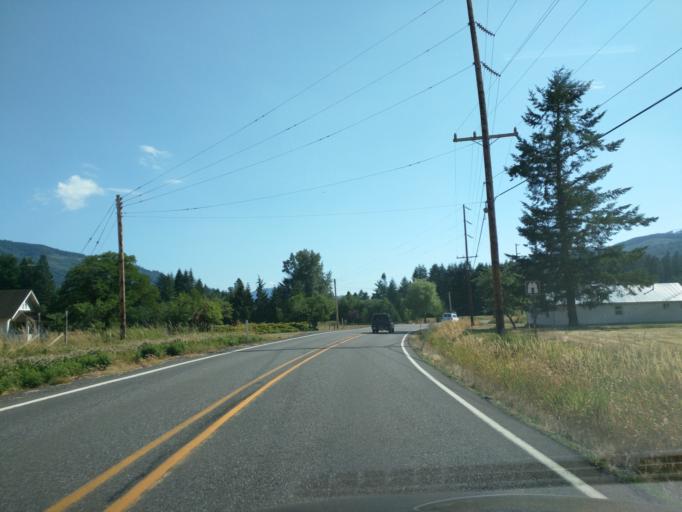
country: US
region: Washington
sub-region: Whatcom County
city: Peaceful Valley
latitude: 48.9010
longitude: -122.1435
